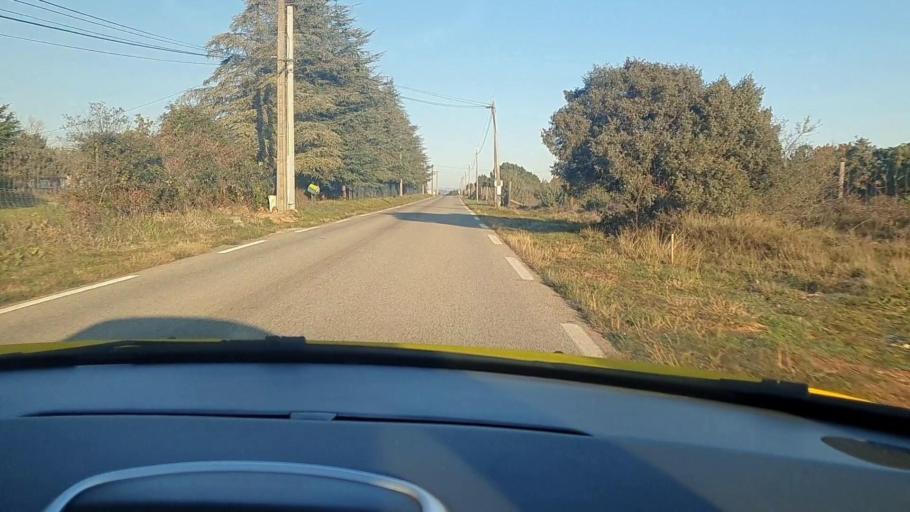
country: FR
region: Languedoc-Roussillon
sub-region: Departement du Gard
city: Montaren-et-Saint-Mediers
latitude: 44.1198
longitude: 4.3692
